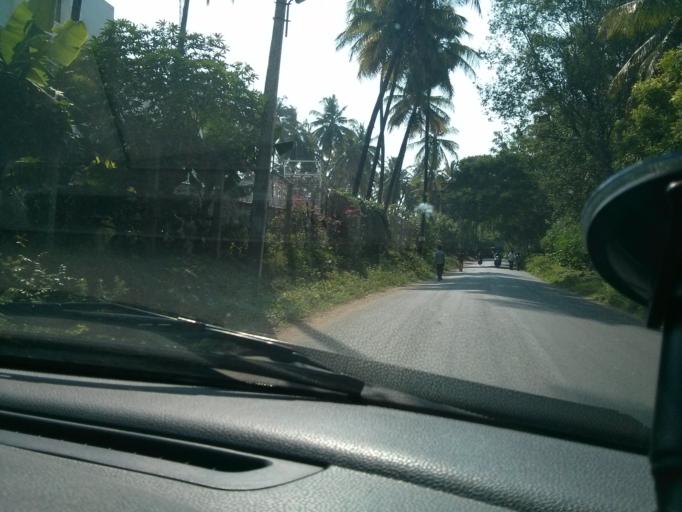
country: IN
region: Tamil Nadu
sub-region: Coimbatore
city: Periyanayakkanpalaiyam
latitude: 11.1028
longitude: 76.9337
